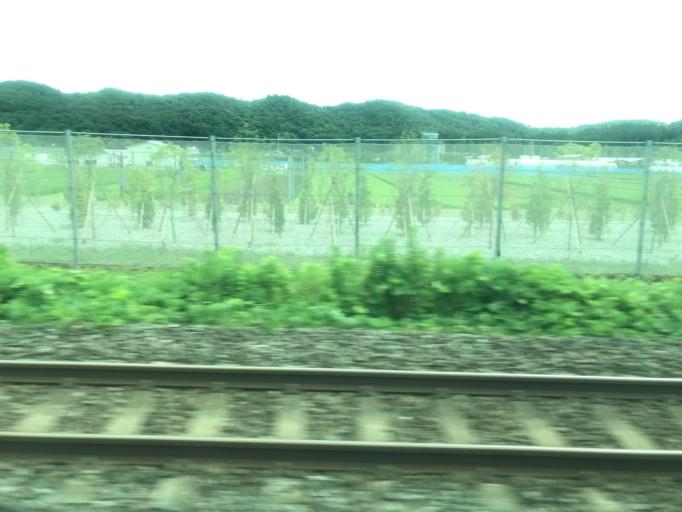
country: JP
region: Fukushima
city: Motomiya
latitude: 37.4764
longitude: 140.3837
